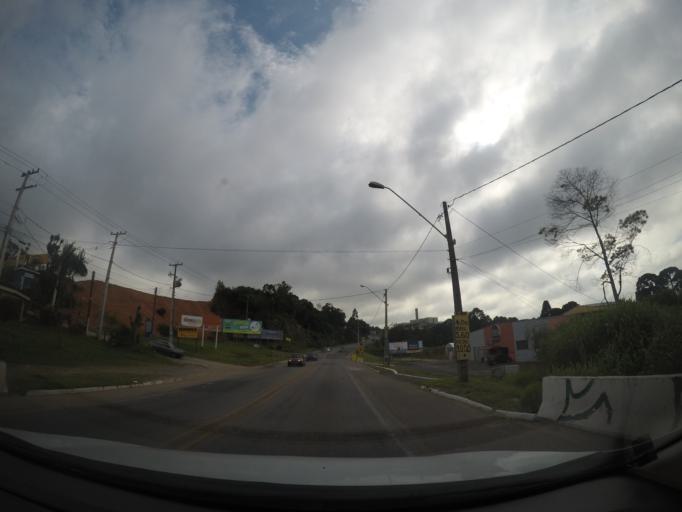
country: BR
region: Parana
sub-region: Colombo
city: Colombo
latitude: -25.3637
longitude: -49.2202
